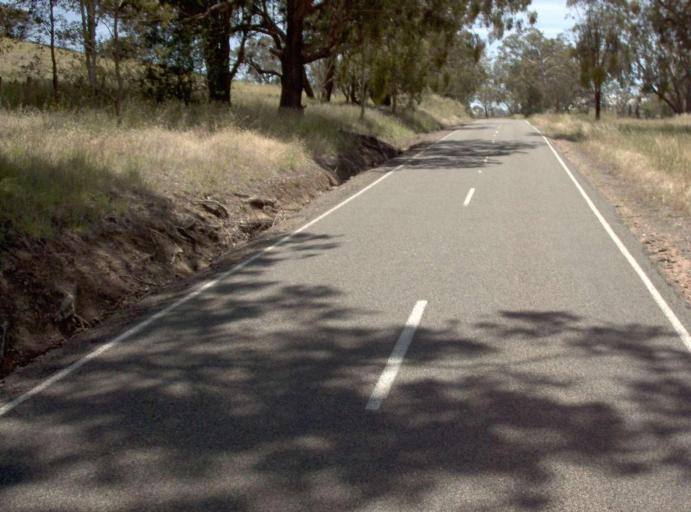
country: AU
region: Victoria
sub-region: East Gippsland
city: Bairnsdale
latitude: -37.4091
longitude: 147.8357
